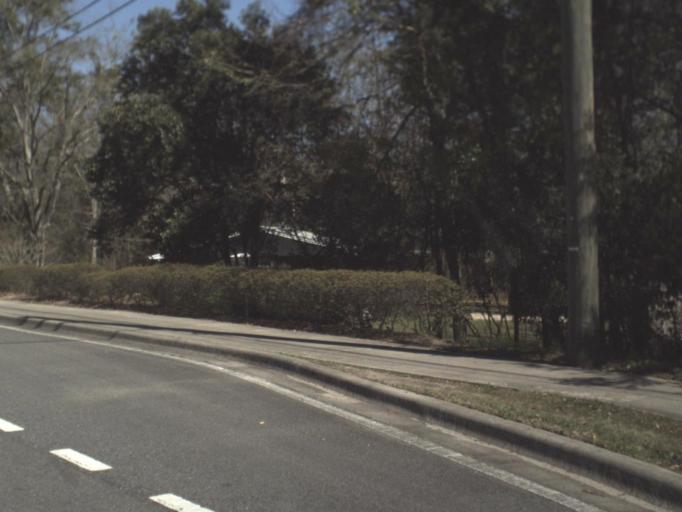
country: US
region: Florida
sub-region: Leon County
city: Tallahassee
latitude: 30.4198
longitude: -84.2302
